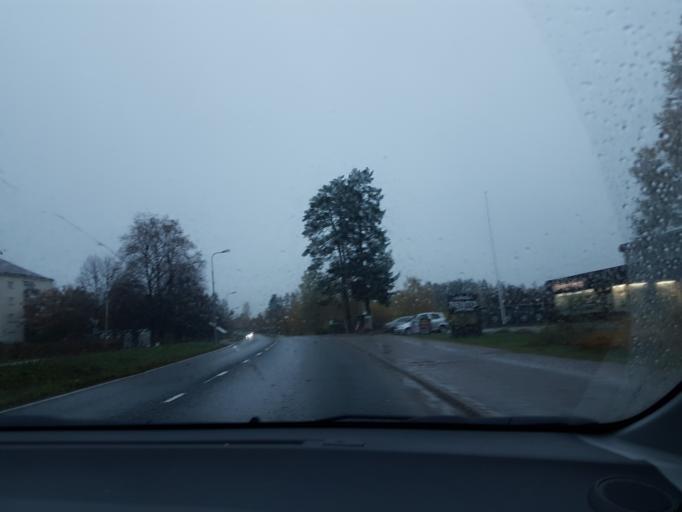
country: FI
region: Uusimaa
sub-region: Helsinki
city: Jaervenpaeae
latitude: 60.5322
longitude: 25.1104
